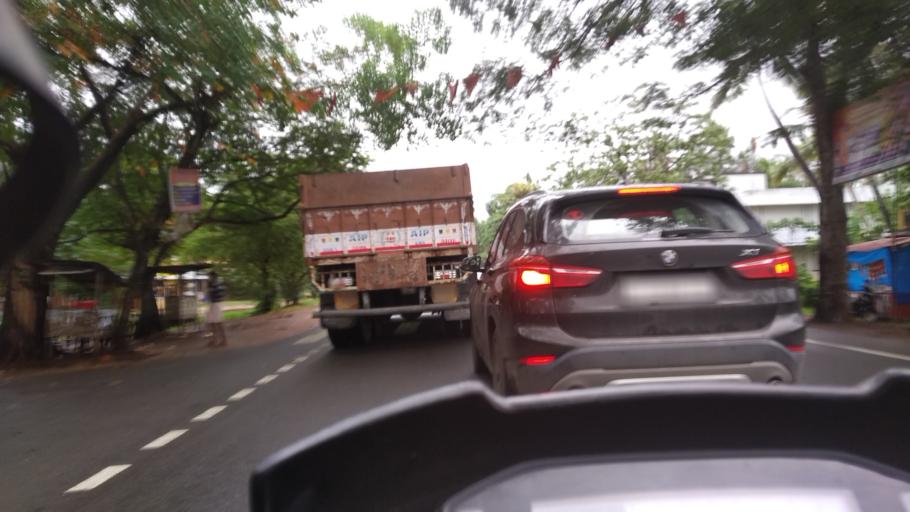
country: IN
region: Kerala
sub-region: Alappuzha
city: Mavelikara
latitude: 9.2950
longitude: 76.4342
